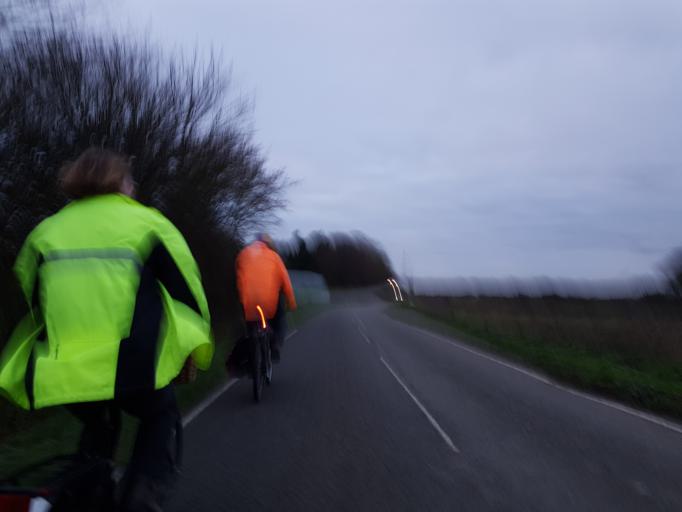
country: GB
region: England
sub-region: Cambridgeshire
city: Fulbourn
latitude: 52.2157
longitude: 0.1920
